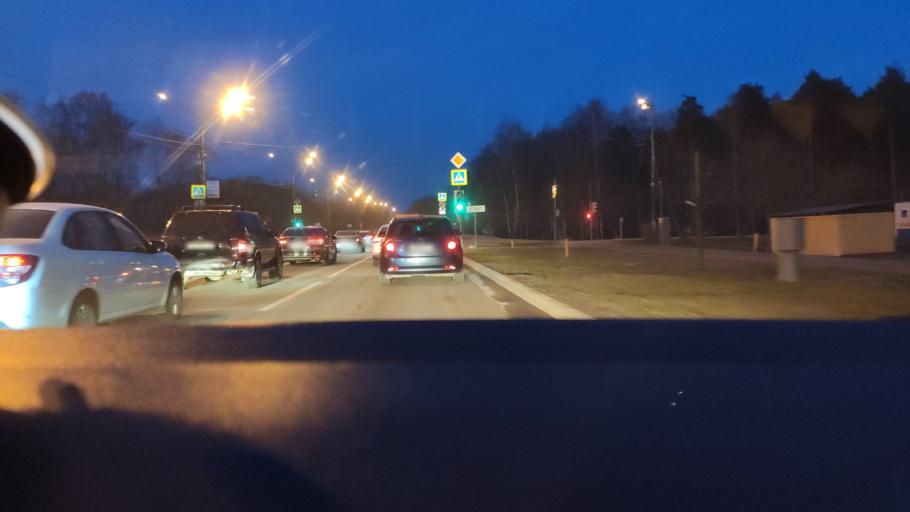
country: RU
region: Moscow
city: Nekrasovka
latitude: 55.6866
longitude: 37.9279
